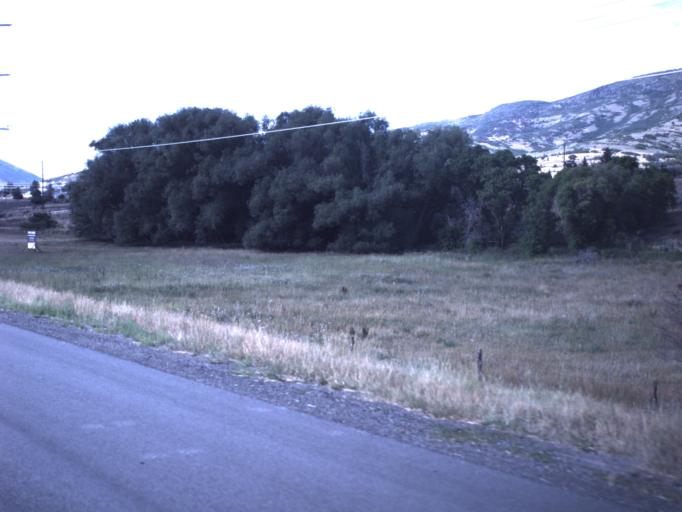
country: US
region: Utah
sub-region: Wasatch County
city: Heber
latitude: 40.5450
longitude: -111.4178
